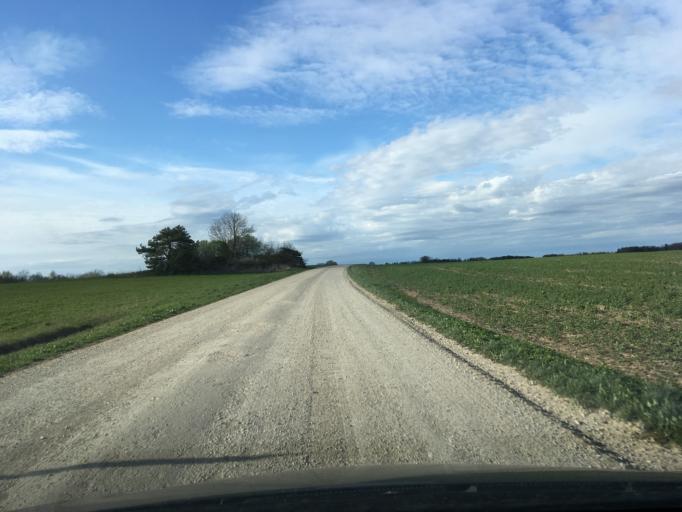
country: EE
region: Raplamaa
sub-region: Maerjamaa vald
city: Marjamaa
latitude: 58.9290
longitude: 24.3068
